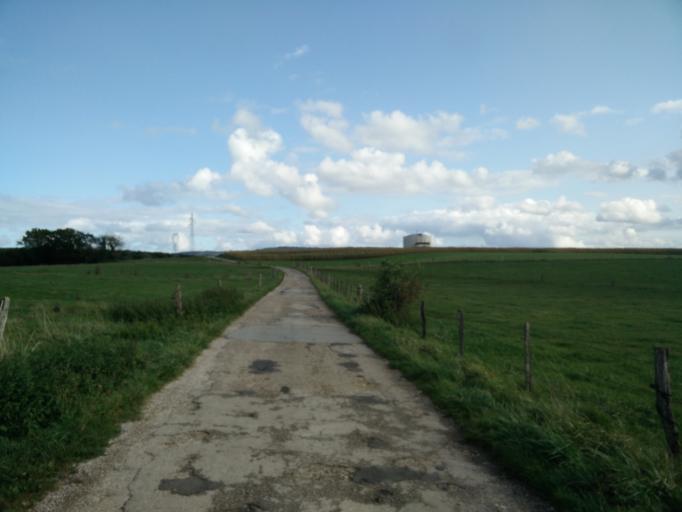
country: FR
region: Franche-Comte
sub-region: Departement du Doubs
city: Saone
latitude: 47.2230
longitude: 6.1276
